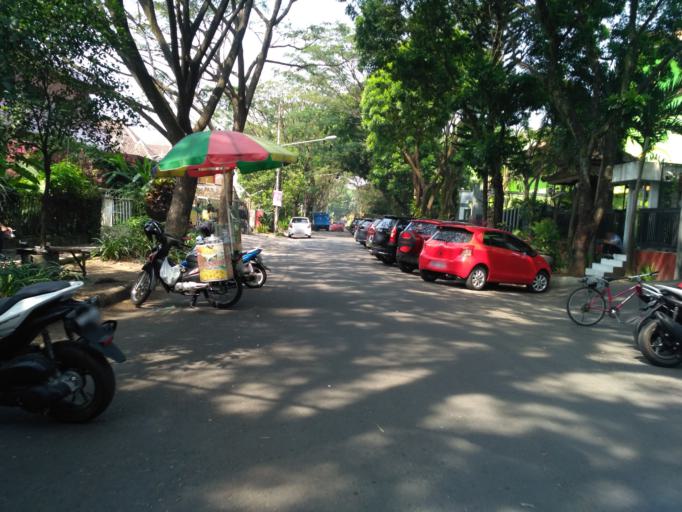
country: ID
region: East Java
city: Malang
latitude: -7.9757
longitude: 112.6356
